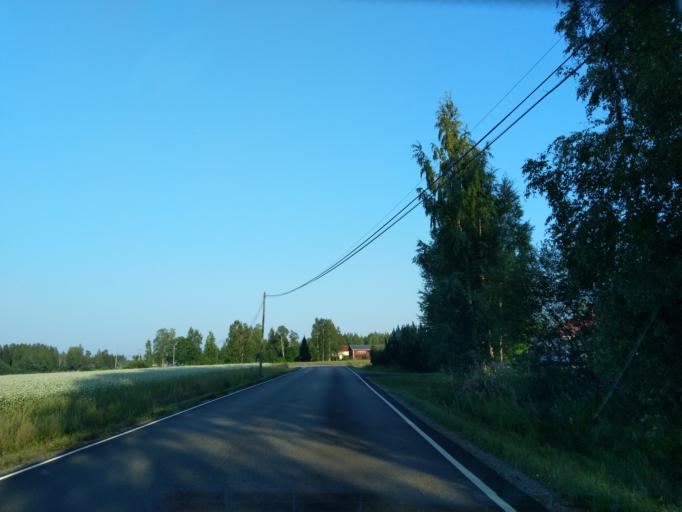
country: FI
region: Satakunta
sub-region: Pohjois-Satakunta
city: Kankaanpaeae
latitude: 61.8171
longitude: 22.3382
